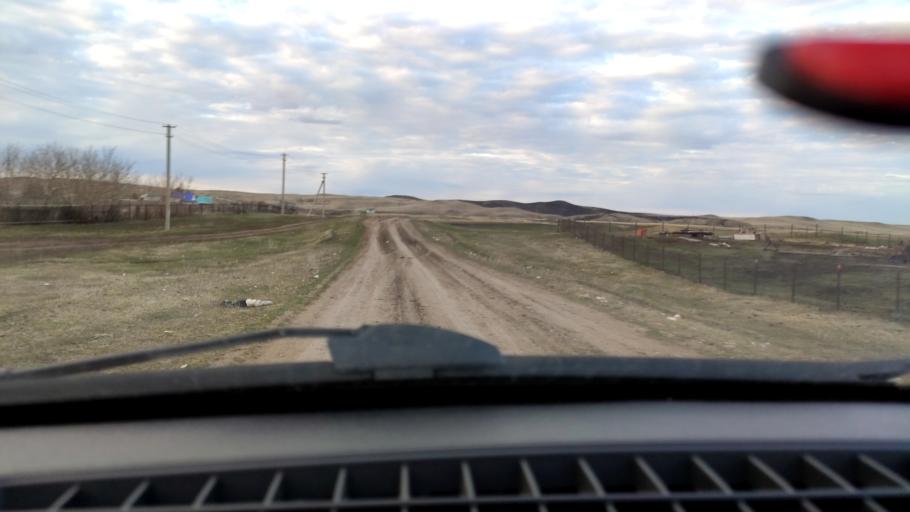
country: RU
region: Bashkortostan
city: Tolbazy
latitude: 54.0151
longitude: 55.5338
